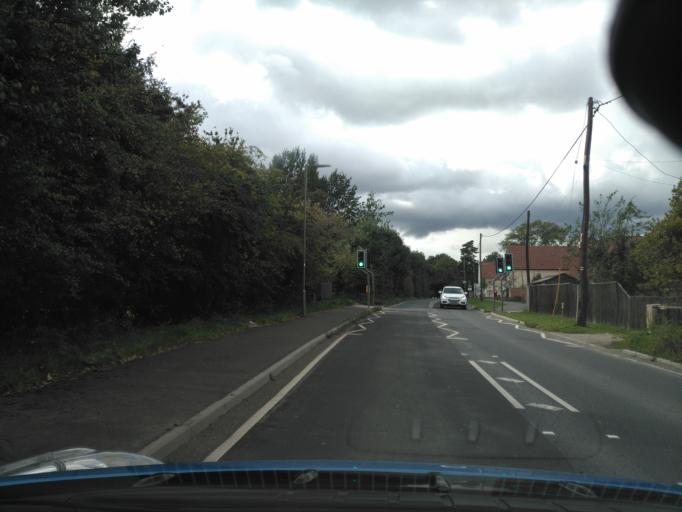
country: GB
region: England
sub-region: Oxfordshire
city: Harwell
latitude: 51.6006
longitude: -1.3369
